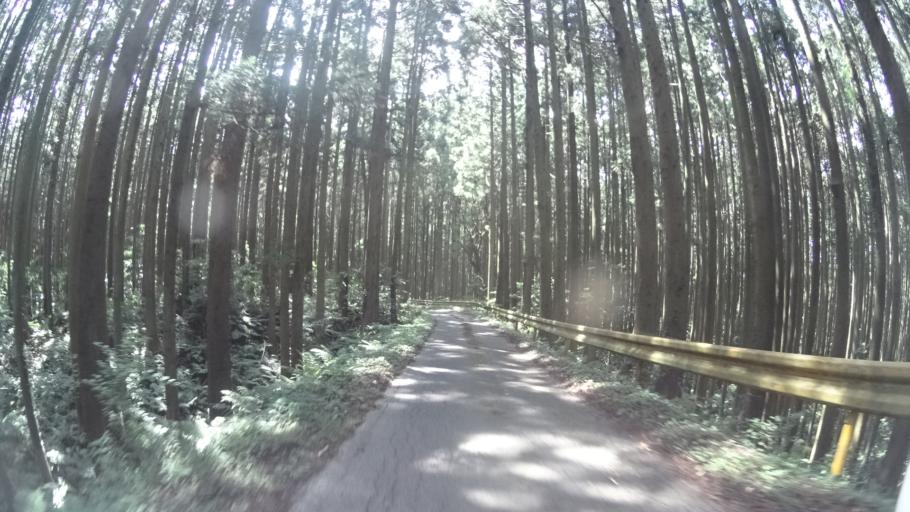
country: JP
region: Yamaguchi
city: Hagi
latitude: 34.4943
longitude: 131.5640
